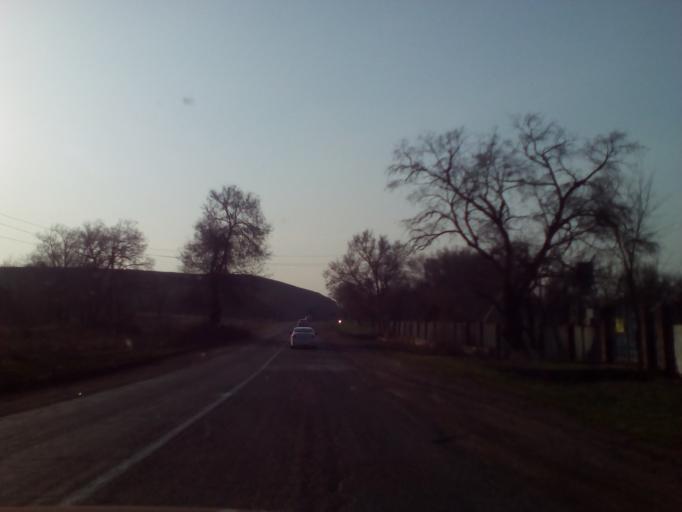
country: KZ
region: Almaty Oblysy
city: Burunday
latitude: 43.1695
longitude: 76.5379
